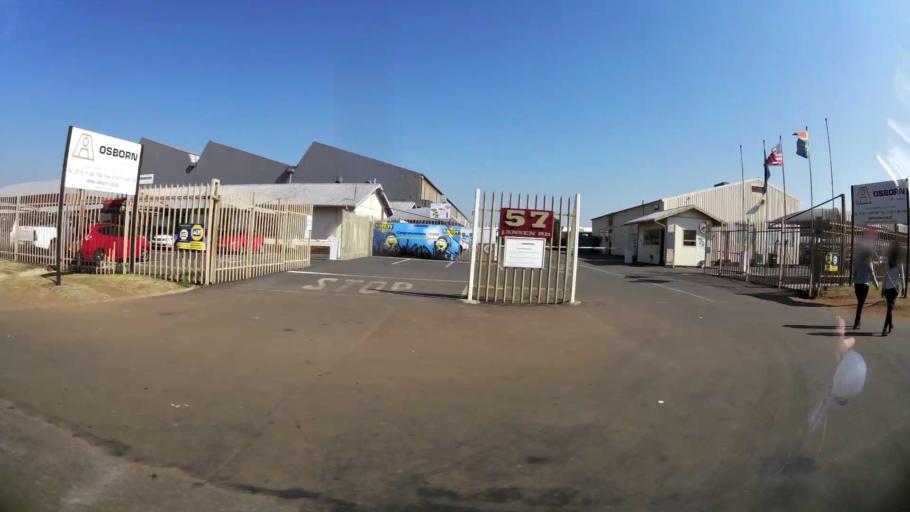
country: ZA
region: Gauteng
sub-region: Ekurhuleni Metropolitan Municipality
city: Boksburg
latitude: -26.1701
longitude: 28.2109
